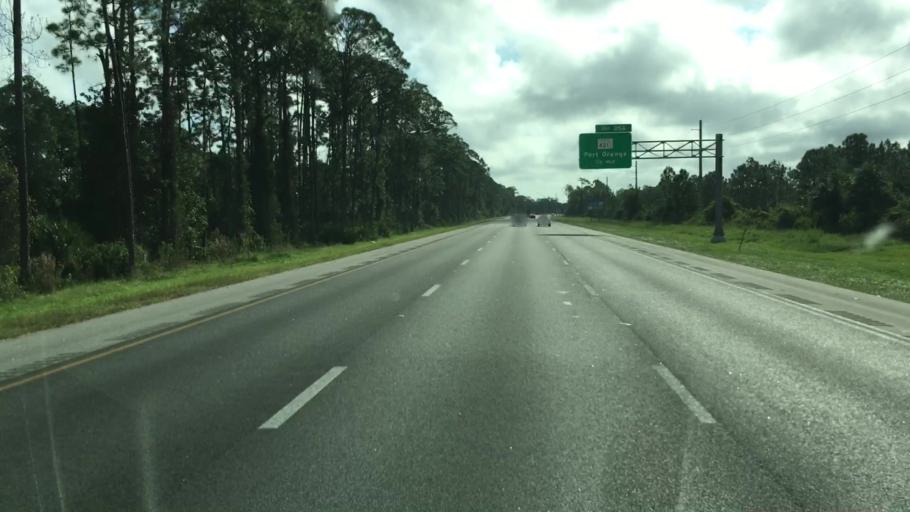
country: US
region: Florida
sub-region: Volusia County
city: Port Orange
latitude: 29.1167
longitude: -81.0388
